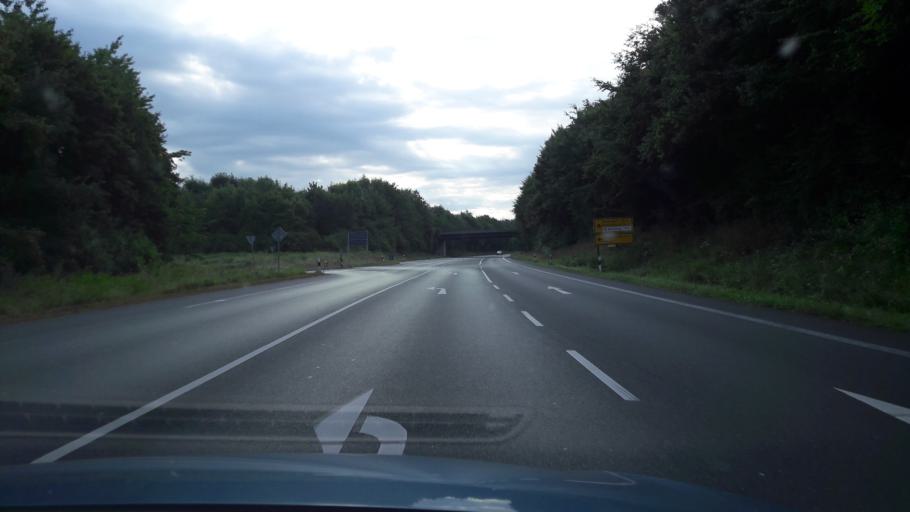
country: DE
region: North Rhine-Westphalia
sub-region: Regierungsbezirk Munster
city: Everswinkel
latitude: 51.9313
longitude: 7.8487
